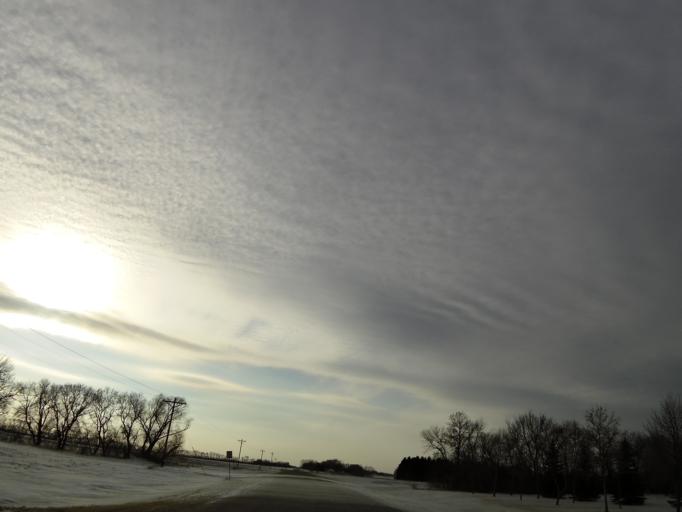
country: US
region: North Dakota
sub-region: Walsh County
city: Grafton
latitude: 48.4267
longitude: -97.3032
